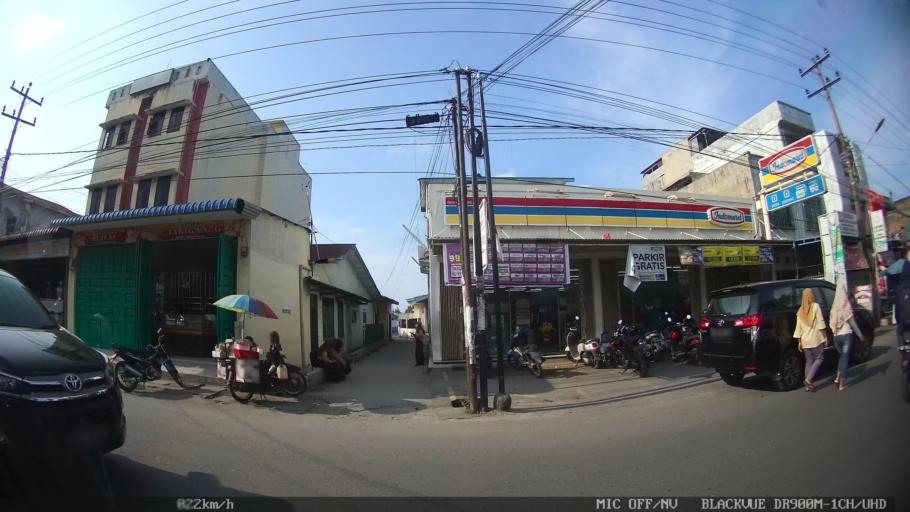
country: ID
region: North Sumatra
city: Medan
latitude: 3.5973
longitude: 98.7499
